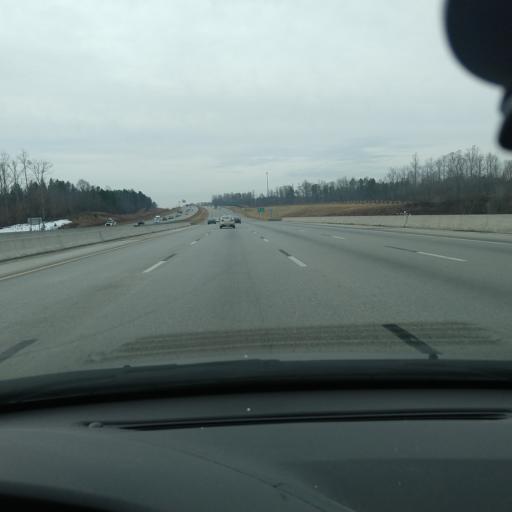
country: US
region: North Carolina
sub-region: Rowan County
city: Spencer
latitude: 35.7175
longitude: -80.3913
